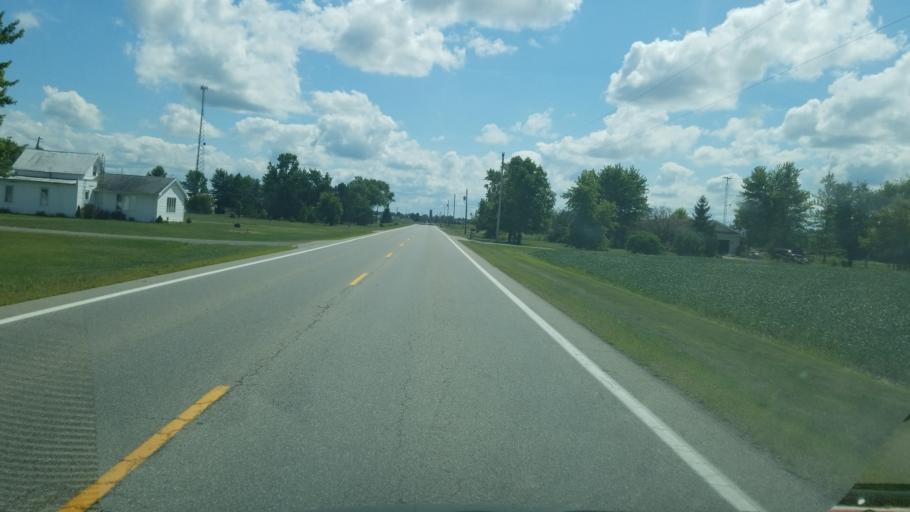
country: US
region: Ohio
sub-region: Putnam County
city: Kalida
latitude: 41.0049
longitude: -84.1979
